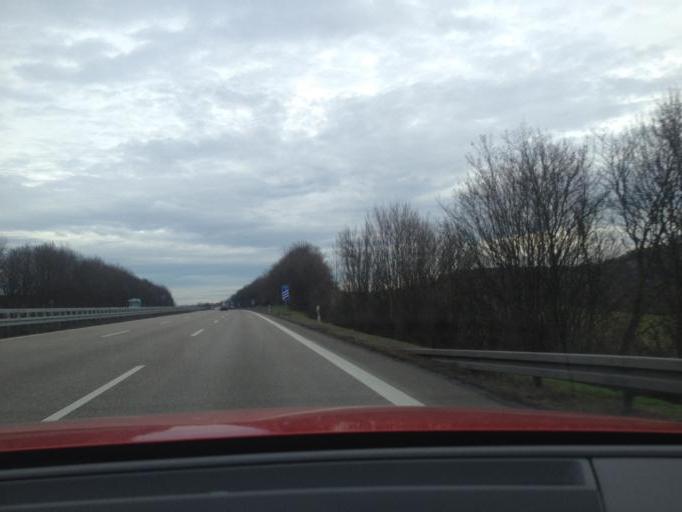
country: DE
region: Baden-Wuerttemberg
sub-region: Regierungsbezirk Stuttgart
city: Waldenburg
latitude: 49.2088
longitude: 9.6279
